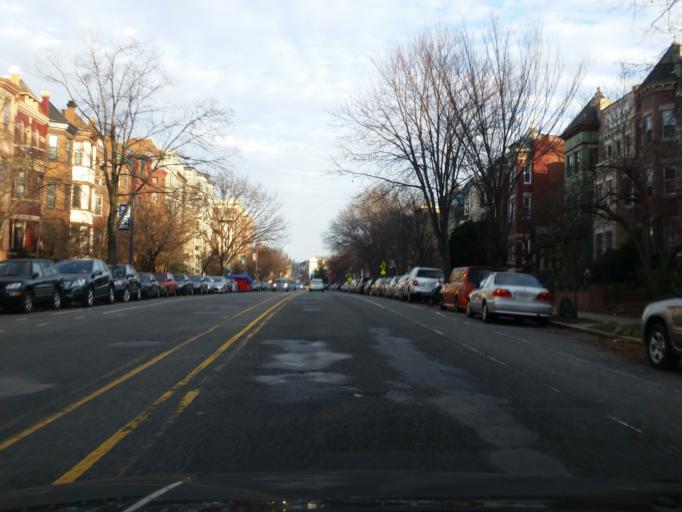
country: US
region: Washington, D.C.
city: Washington, D.C.
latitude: 38.9233
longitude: -77.0466
